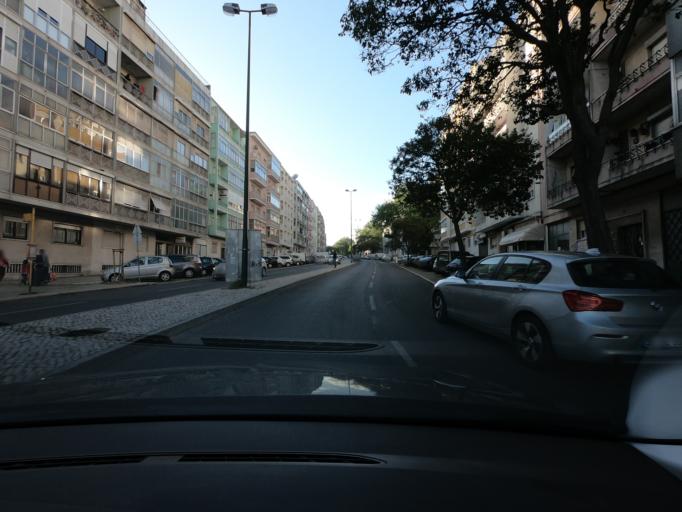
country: PT
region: Lisbon
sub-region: Lisbon
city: Lisbon
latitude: 38.7283
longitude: -9.1244
